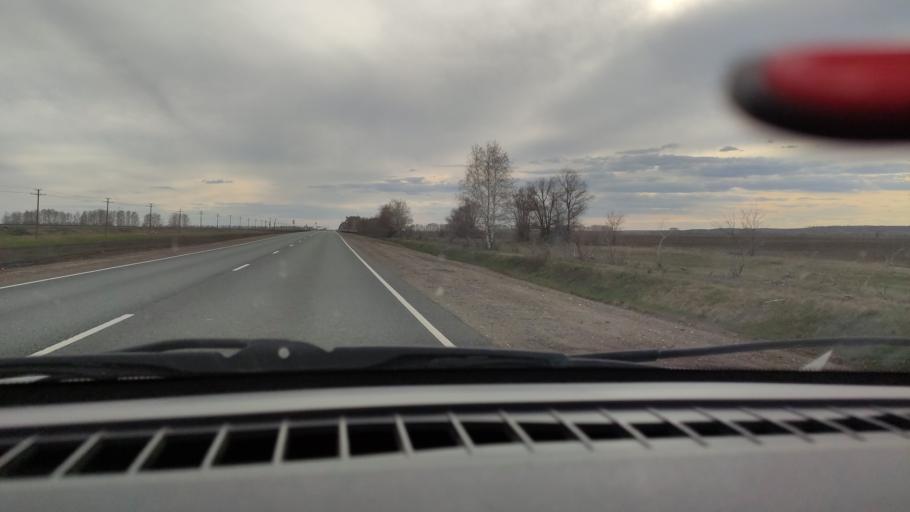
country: RU
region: Bashkortostan
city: Mayachnyy
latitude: 52.3843
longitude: 55.6600
